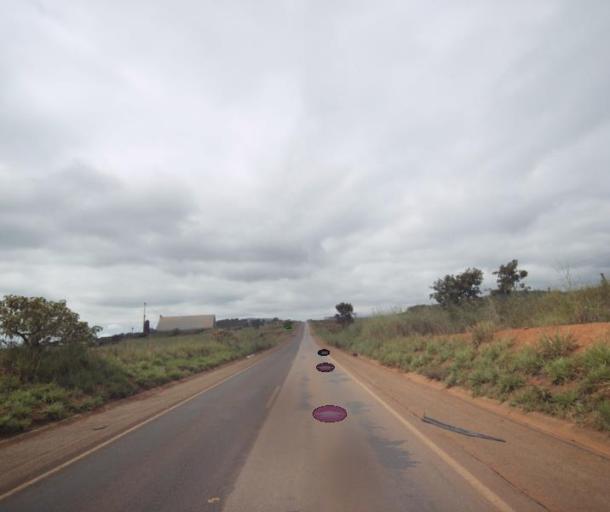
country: BR
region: Goias
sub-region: Barro Alto
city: Barro Alto
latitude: -14.9571
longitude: -48.9320
